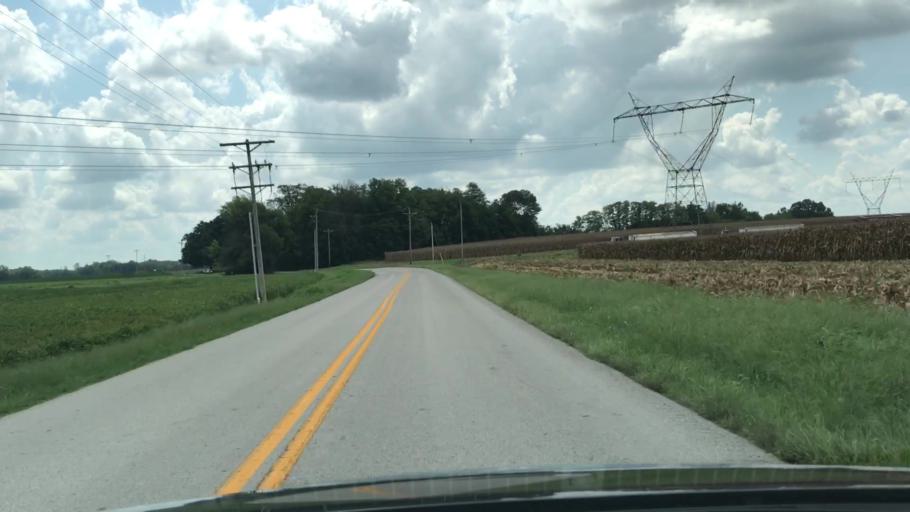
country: US
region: Kentucky
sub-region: Todd County
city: Elkton
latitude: 36.7730
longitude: -87.1177
